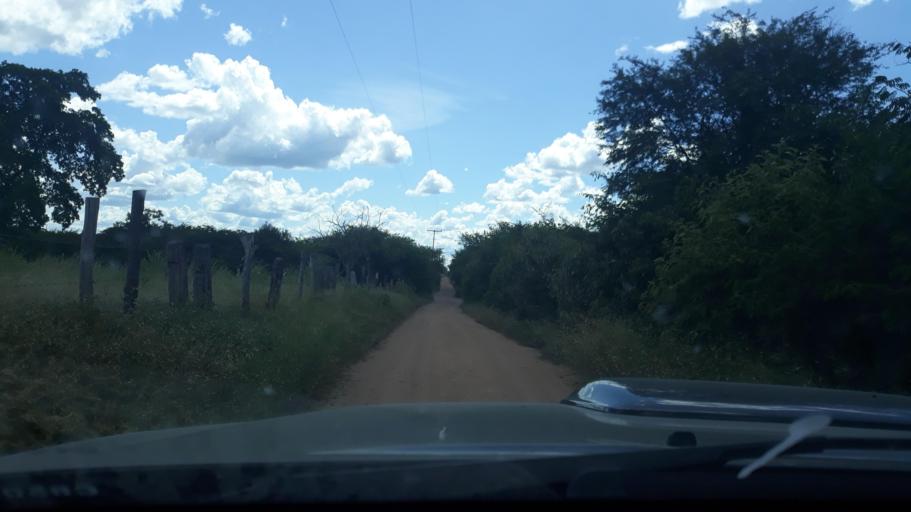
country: BR
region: Bahia
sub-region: Riacho De Santana
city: Riacho de Santana
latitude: -13.8628
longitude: -43.0256
